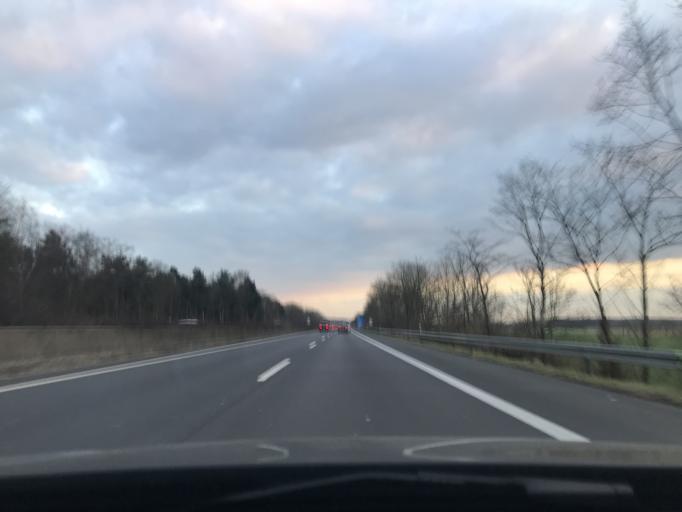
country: DE
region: North Rhine-Westphalia
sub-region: Regierungsbezirk Koln
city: Sinnersdorf
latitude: 51.0570
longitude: 6.8336
